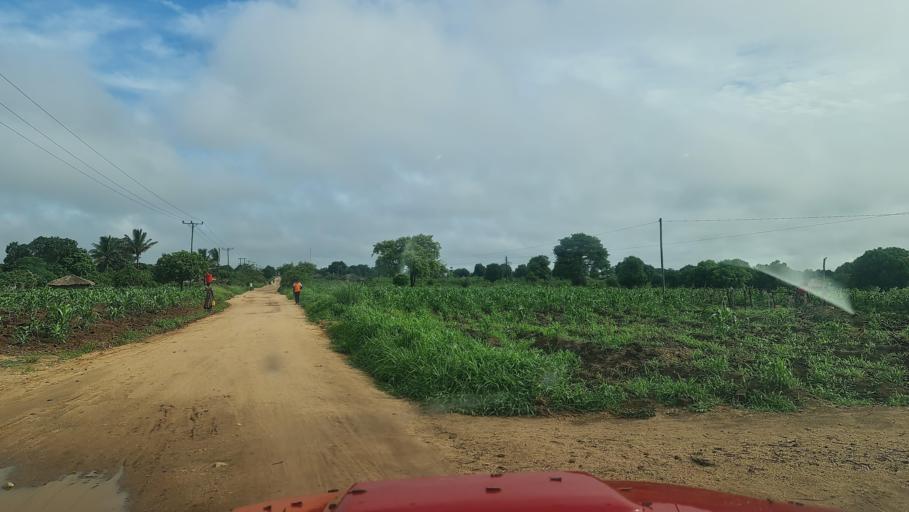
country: MW
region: Southern Region
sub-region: Nsanje District
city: Nsanje
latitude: -17.3108
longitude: 35.5928
